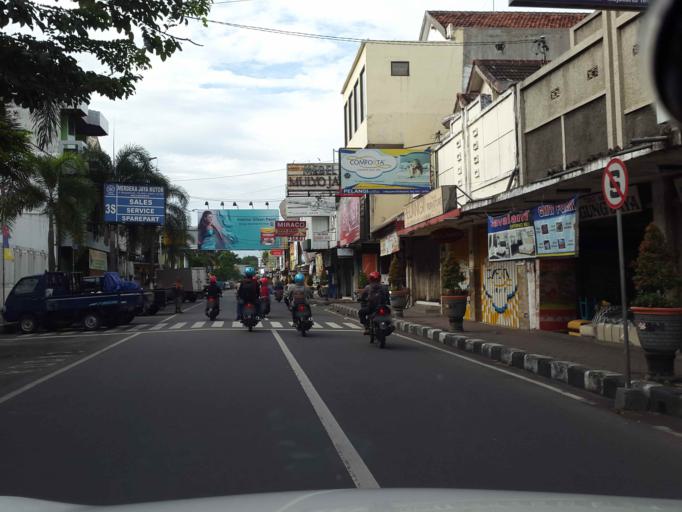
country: ID
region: East Java
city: Mojokerto
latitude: -7.4687
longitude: 112.4320
